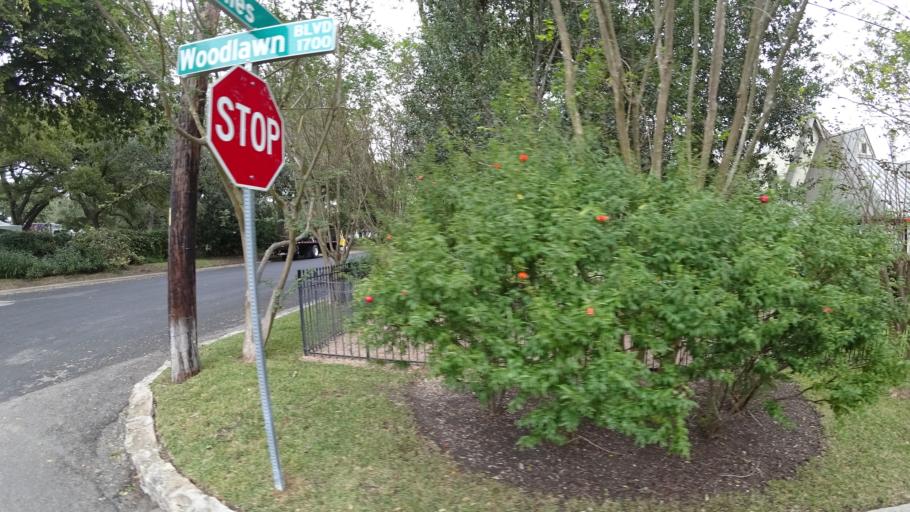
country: US
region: Texas
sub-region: Travis County
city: Austin
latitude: 30.2863
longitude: -97.7587
